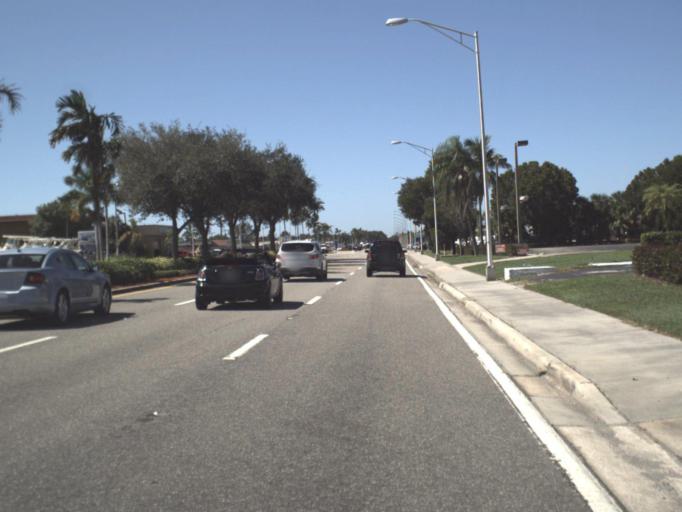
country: US
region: Florida
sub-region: Collier County
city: Naples
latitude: 26.1385
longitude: -81.7734
